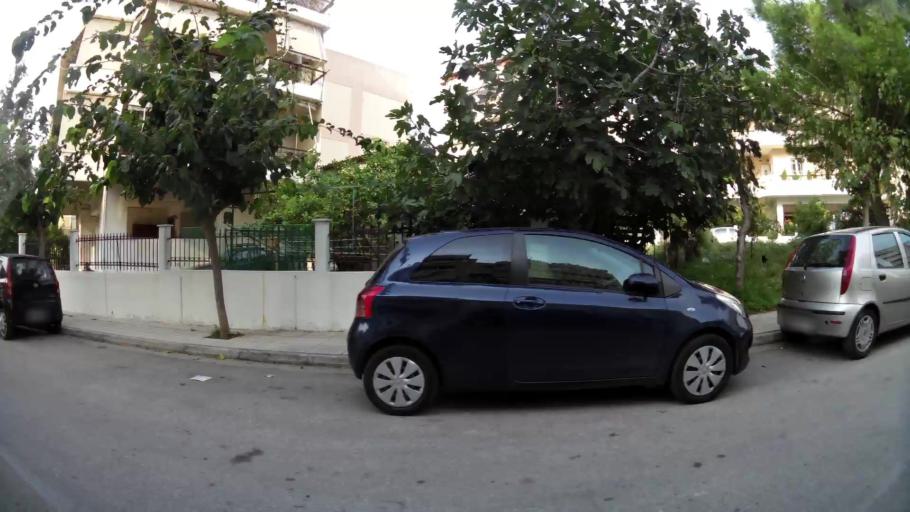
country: GR
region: Attica
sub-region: Nomarchia Athinas
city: Agios Dimitrios
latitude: 37.9296
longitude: 23.7235
